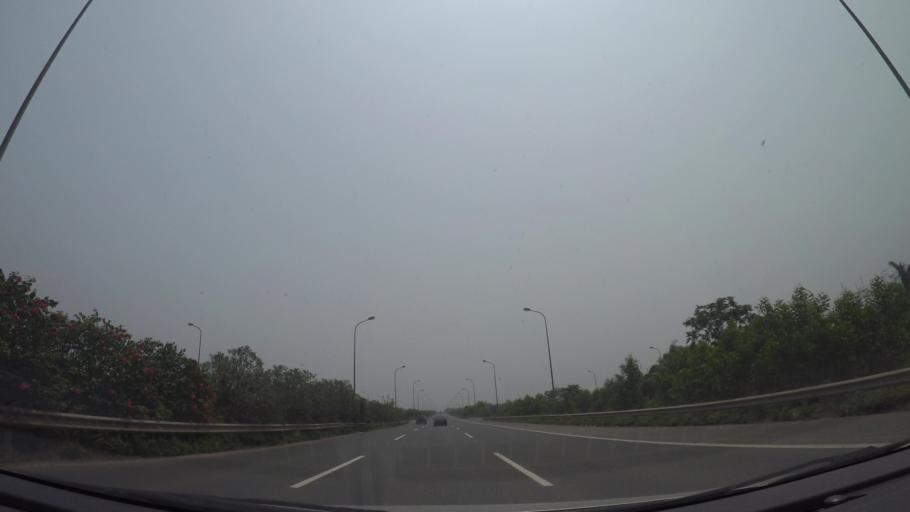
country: VN
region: Ha Noi
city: Lien Quan
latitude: 20.9896
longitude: 105.5610
